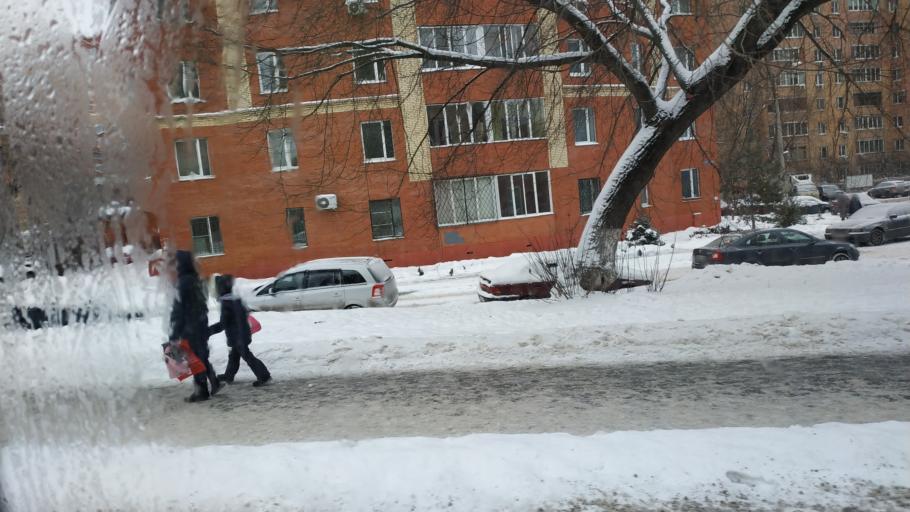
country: RU
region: Moskovskaya
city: Shchelkovo
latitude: 55.9175
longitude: 37.9971
